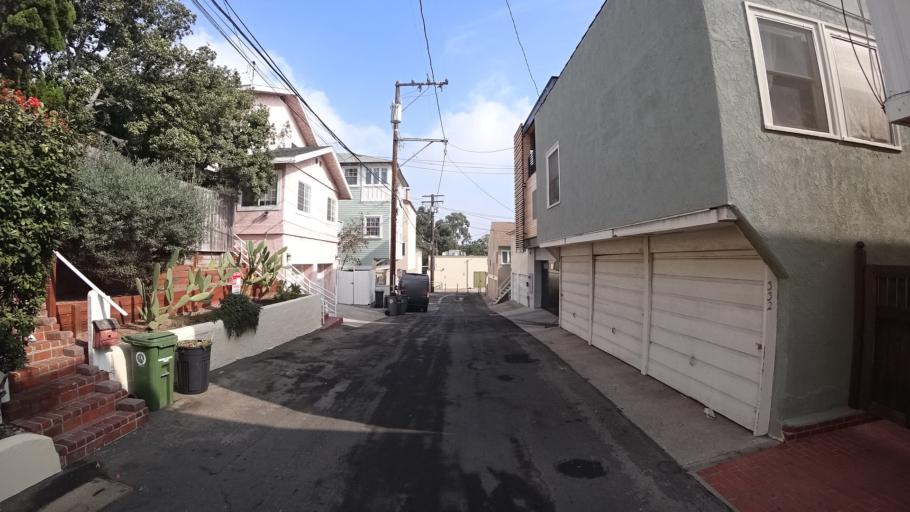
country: US
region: California
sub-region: Los Angeles County
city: Manhattan Beach
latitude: 33.8887
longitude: -118.4109
